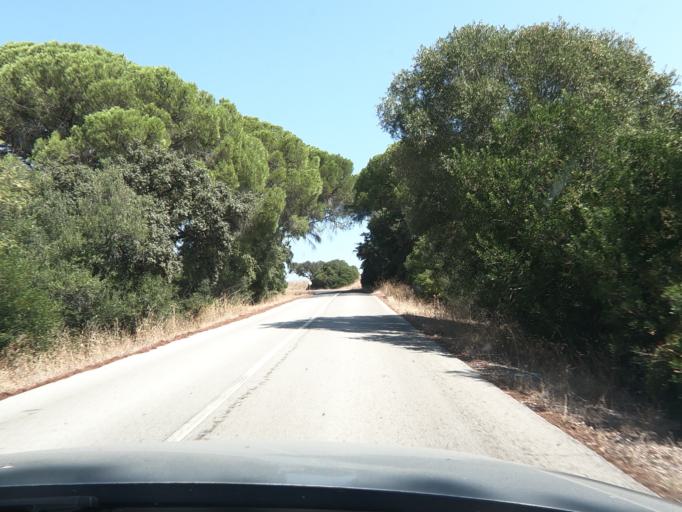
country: PT
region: Setubal
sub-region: Alcacer do Sal
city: Alcacer do Sal
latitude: 38.2904
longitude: -8.4040
